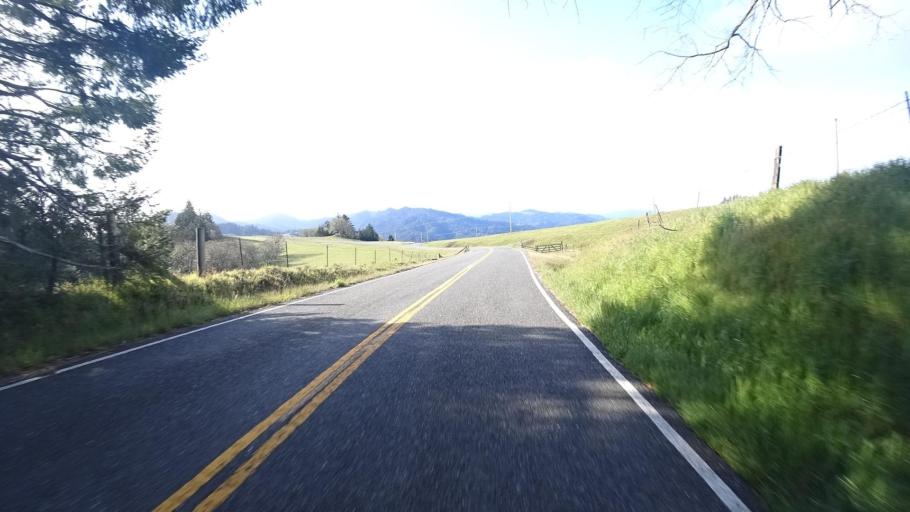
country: US
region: California
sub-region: Humboldt County
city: Blue Lake
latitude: 40.7223
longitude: -123.9433
